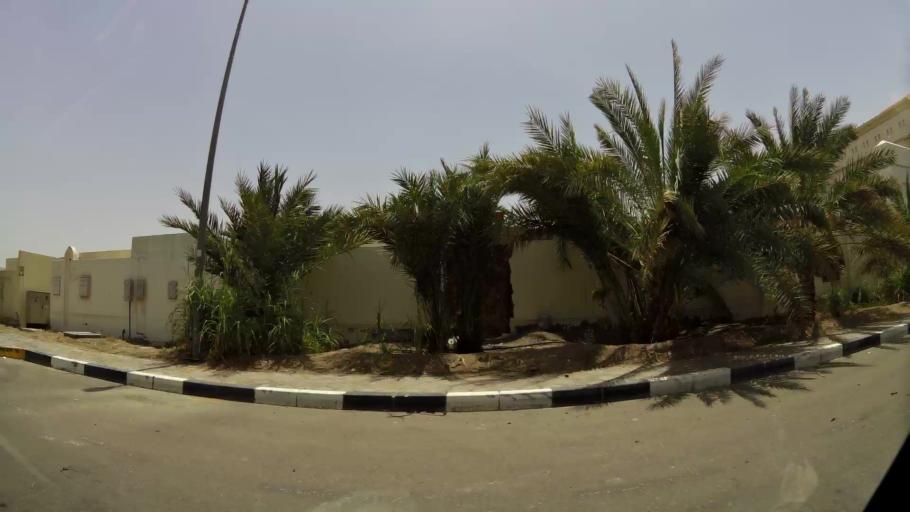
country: AE
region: Abu Dhabi
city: Al Ain
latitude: 24.1950
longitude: 55.7388
